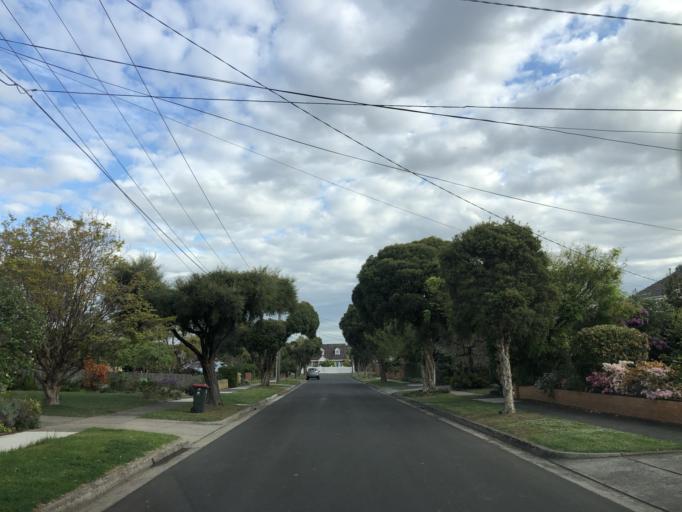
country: AU
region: Victoria
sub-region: Monash
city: Ashwood
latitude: -37.8641
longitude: 145.1170
